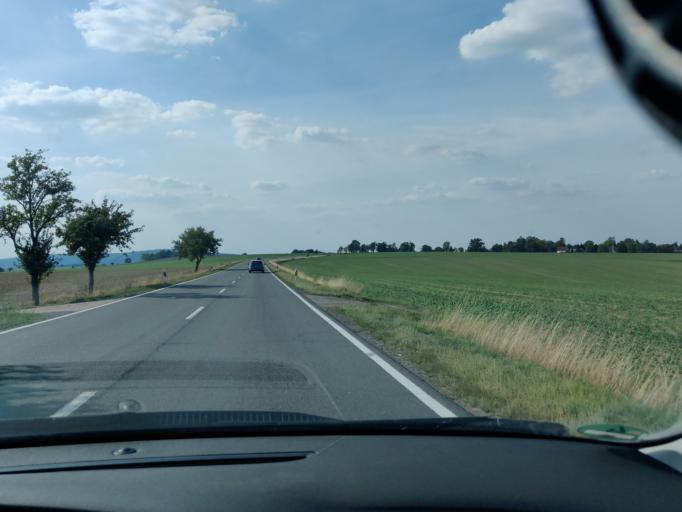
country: DE
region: Saxony
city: Seelitz
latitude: 51.0151
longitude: 12.8678
